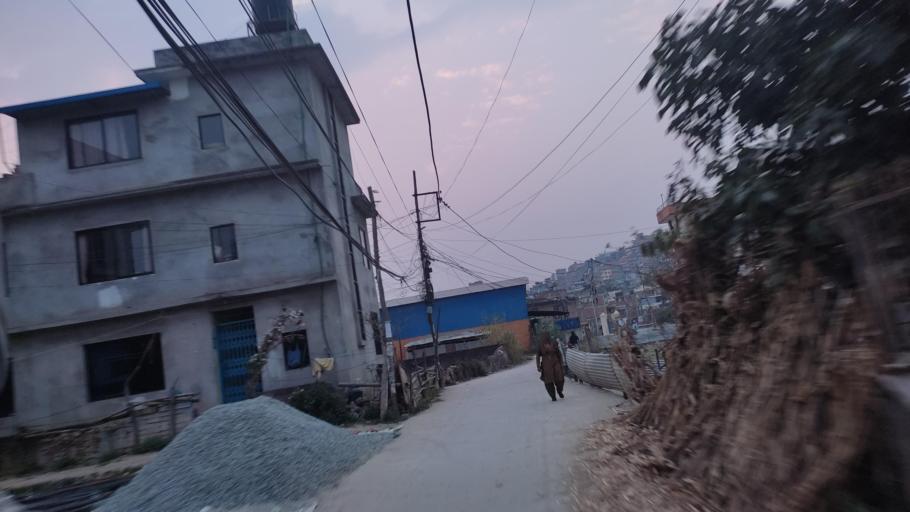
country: NP
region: Central Region
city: Kirtipur
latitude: 27.6723
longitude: 85.2829
